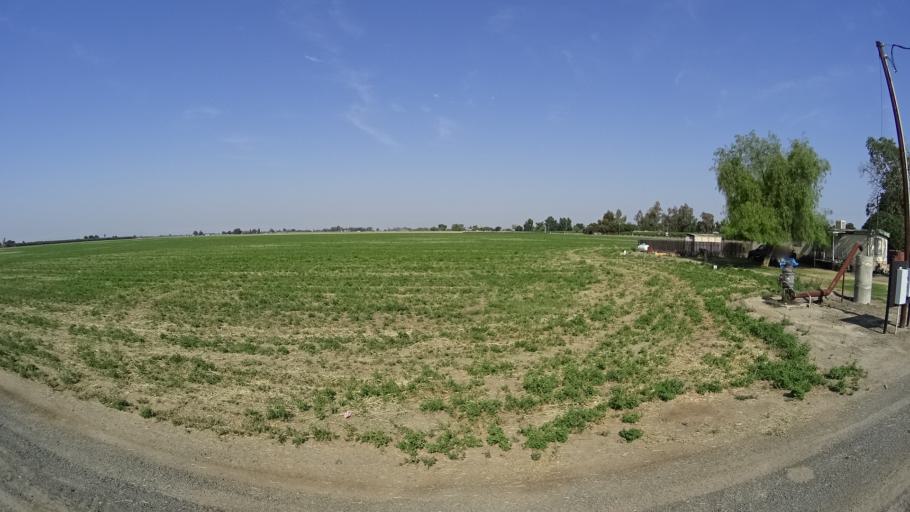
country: US
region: California
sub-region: Kings County
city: Lemoore
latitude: 36.3431
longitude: -119.8513
